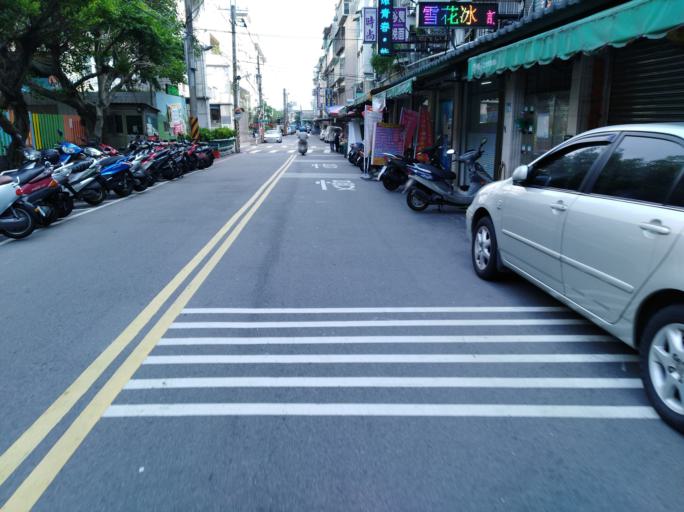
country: TW
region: Taipei
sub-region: Taipei
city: Banqiao
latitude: 25.0449
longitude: 121.4261
